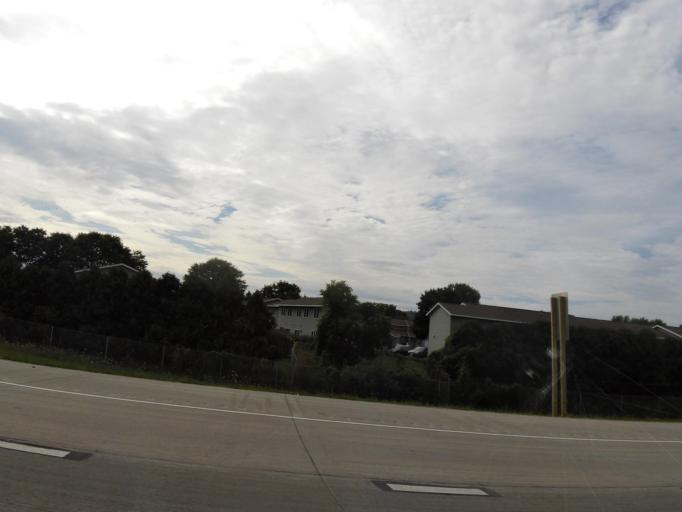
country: US
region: Wisconsin
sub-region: La Crosse County
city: Onalaska
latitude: 43.8769
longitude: -91.2001
